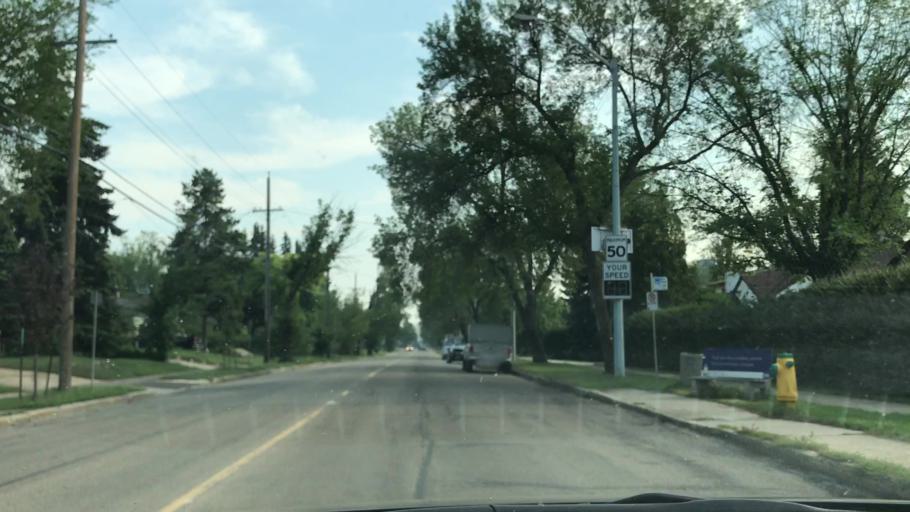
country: CA
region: Alberta
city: Edmonton
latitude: 53.4971
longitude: -113.5120
